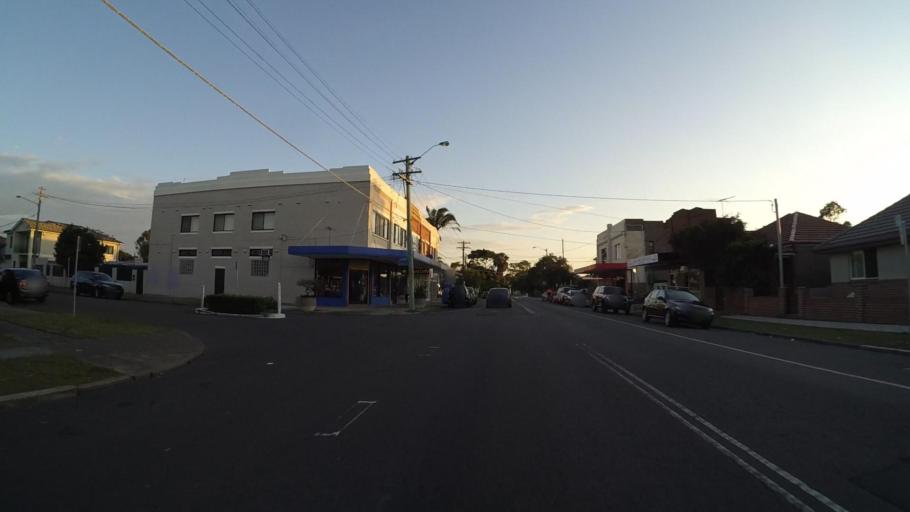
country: AU
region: New South Wales
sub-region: Botany Bay
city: Mascot
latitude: -33.9304
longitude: 151.2054
